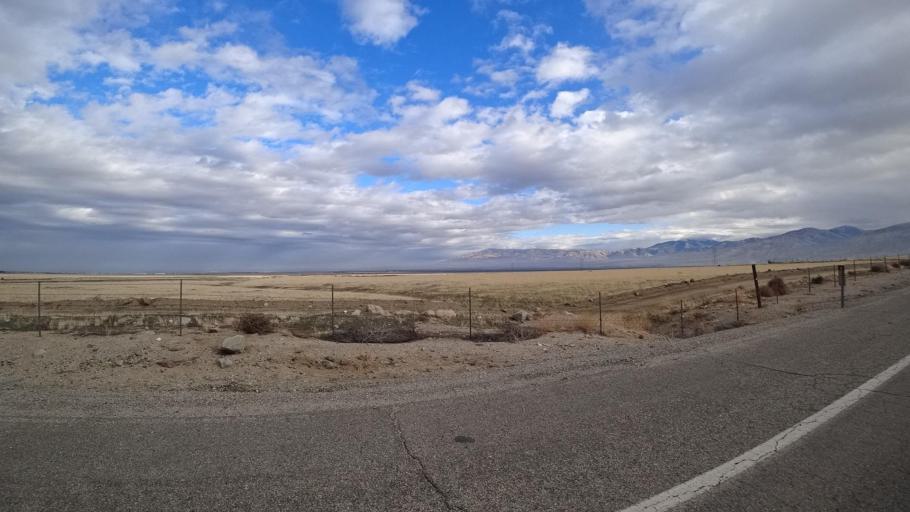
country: US
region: California
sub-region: Kern County
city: Lebec
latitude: 34.9415
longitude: -118.9266
